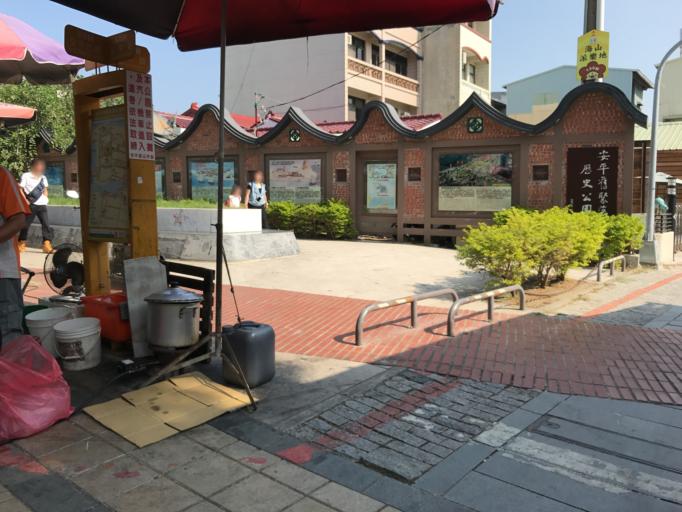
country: TW
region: Taiwan
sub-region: Tainan
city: Tainan
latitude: 23.0013
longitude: 120.1616
